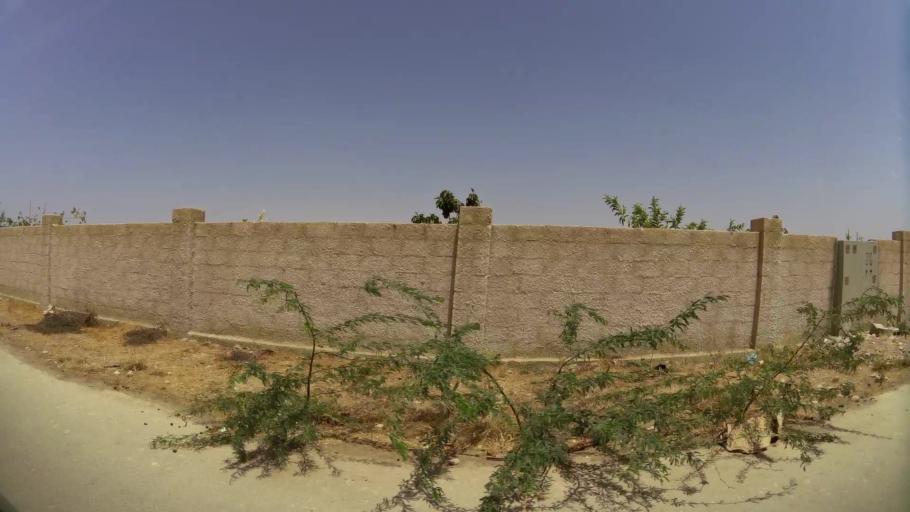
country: OM
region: Zufar
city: Salalah
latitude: 17.0879
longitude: 54.1860
